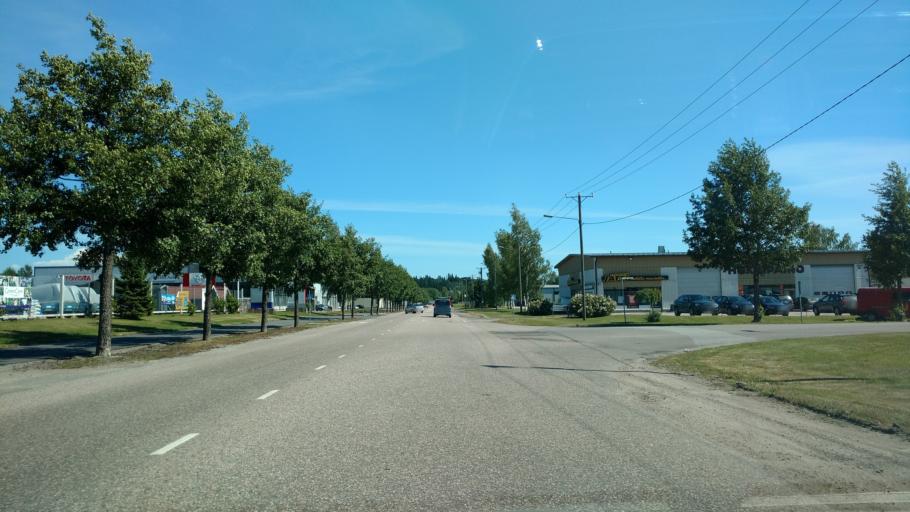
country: FI
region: Varsinais-Suomi
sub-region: Salo
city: Salo
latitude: 60.3840
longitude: 23.1073
